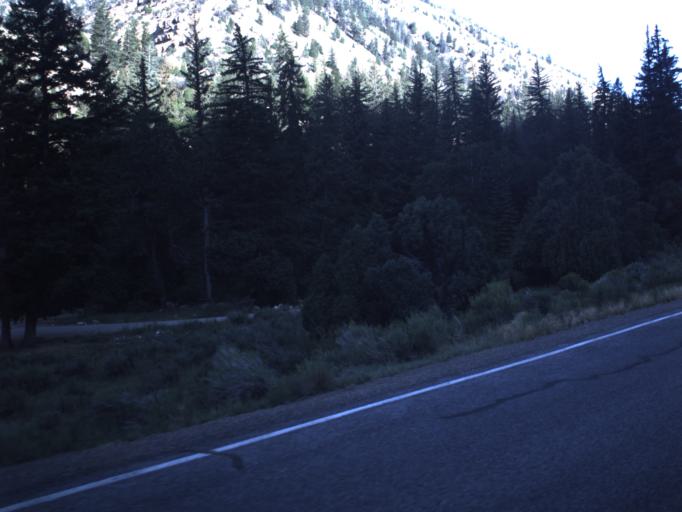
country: US
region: Utah
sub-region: Emery County
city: Huntington
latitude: 39.4434
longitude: -111.1357
